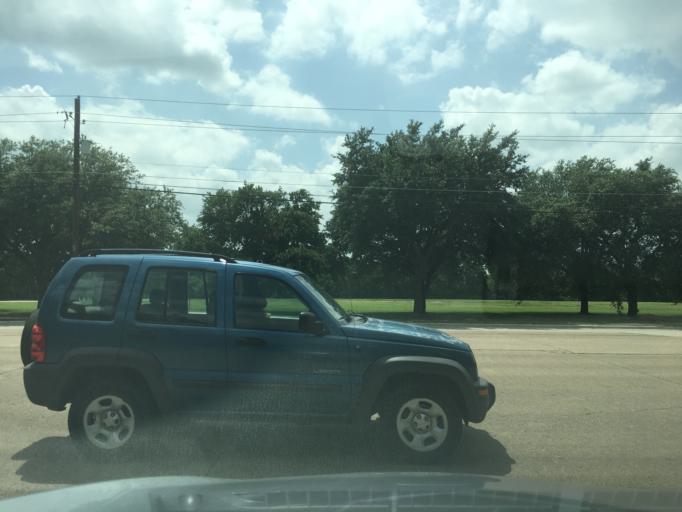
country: US
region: Texas
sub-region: Dallas County
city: Addison
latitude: 32.9083
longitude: -96.8157
